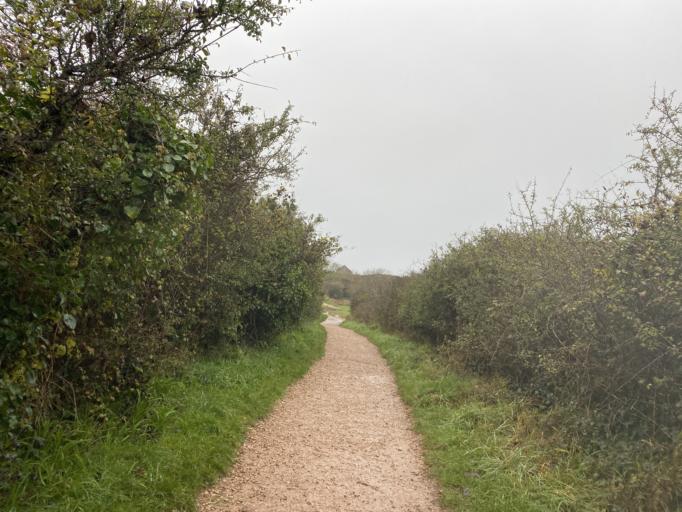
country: GB
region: England
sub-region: Borough of Torbay
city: Brixham
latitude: 50.3974
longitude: -3.4899
